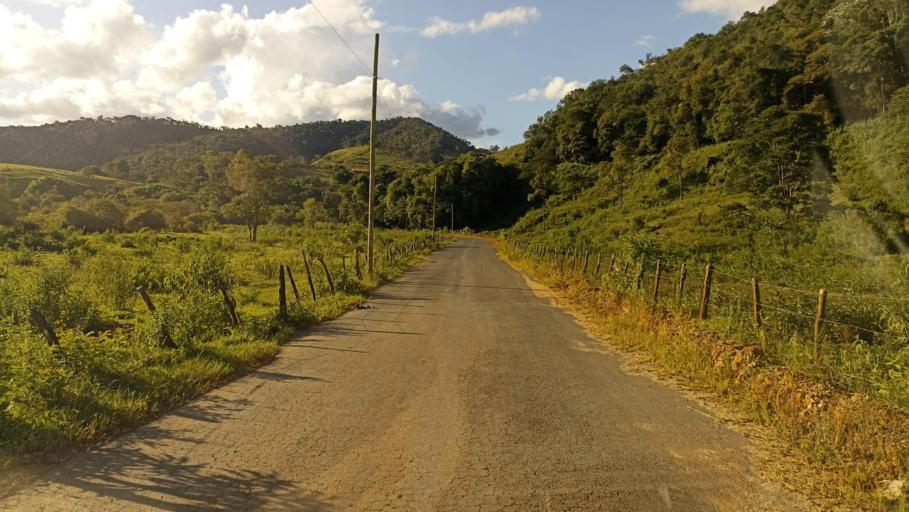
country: BR
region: Minas Gerais
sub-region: Ouro Preto
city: Ouro Preto
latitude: -20.3122
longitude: -43.5976
